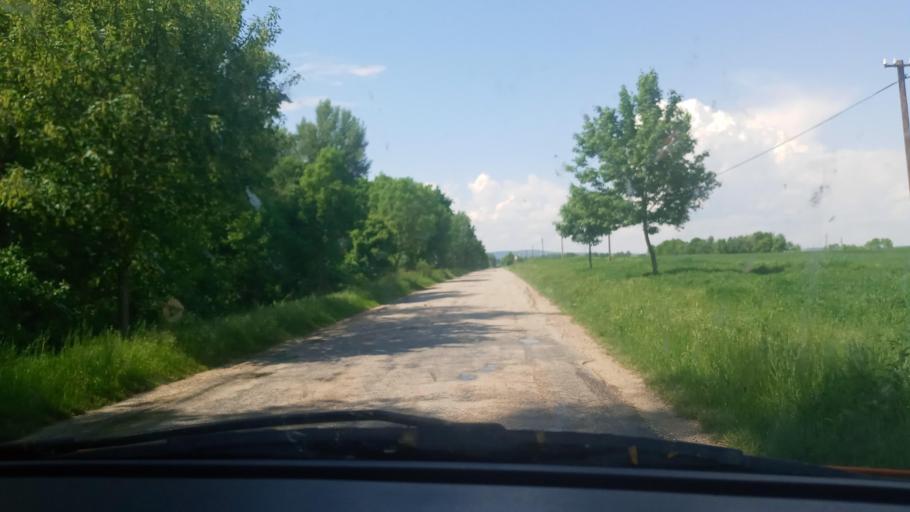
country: HU
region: Baranya
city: Siklos
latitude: 45.8017
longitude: 18.3466
